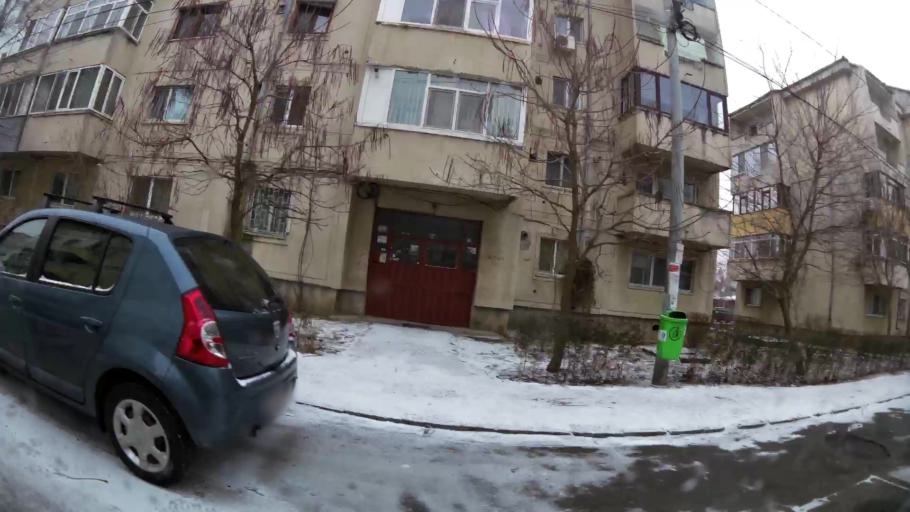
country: RO
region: Dambovita
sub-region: Municipiul Targoviste
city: Targoviste
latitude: 44.9353
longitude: 25.4450
